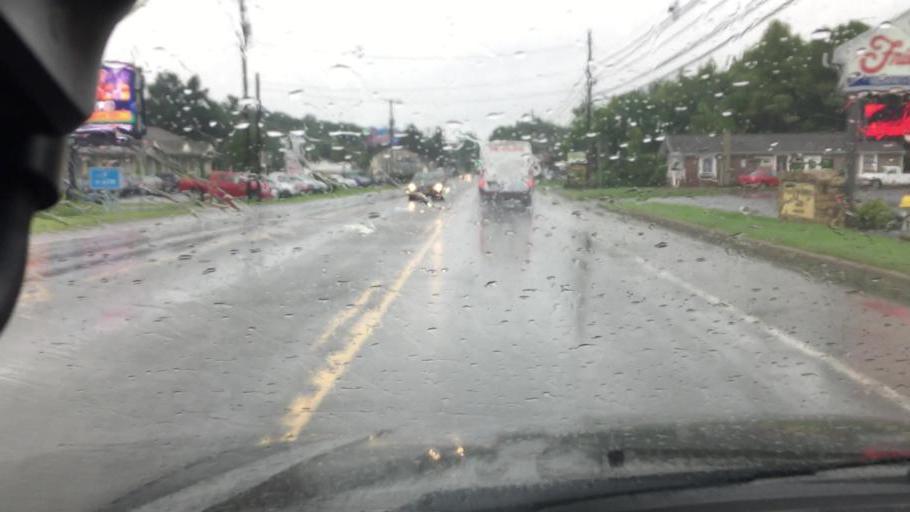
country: US
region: Pennsylvania
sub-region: Monroe County
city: Tannersville
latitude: 41.0337
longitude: -75.3024
